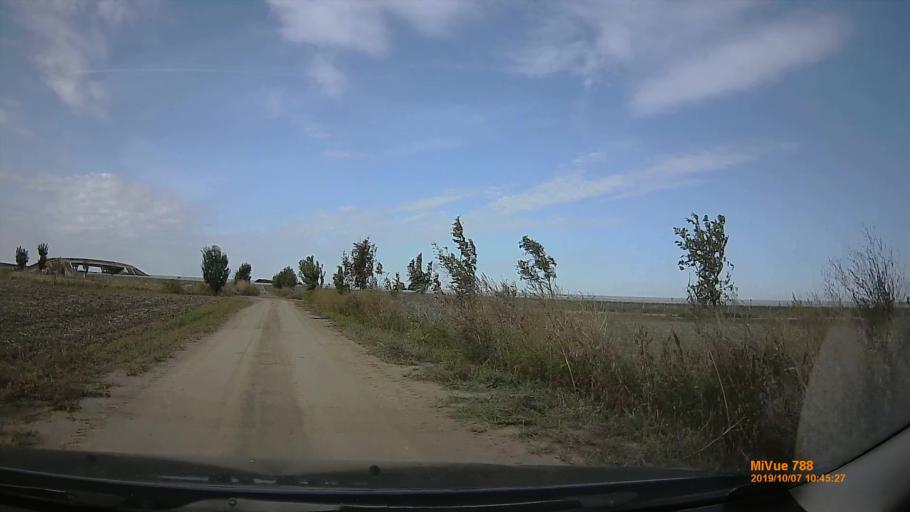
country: HU
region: Bekes
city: Kondoros
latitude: 46.7388
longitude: 20.8199
